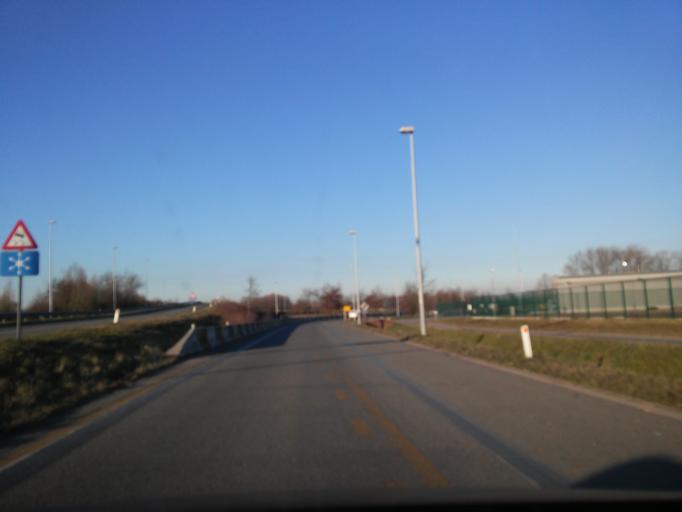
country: BE
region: Flanders
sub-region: Provincie Oost-Vlaanderen
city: Eeklo
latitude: 51.2066
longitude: 3.5358
